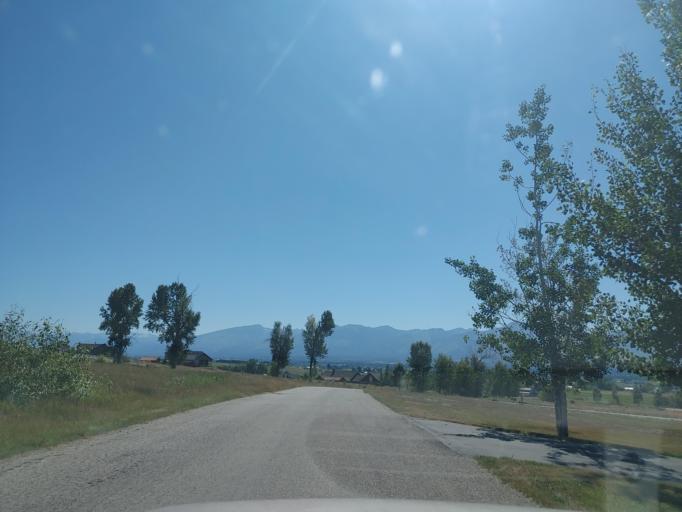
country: US
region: Montana
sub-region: Ravalli County
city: Hamilton
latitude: 46.3487
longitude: -114.0551
